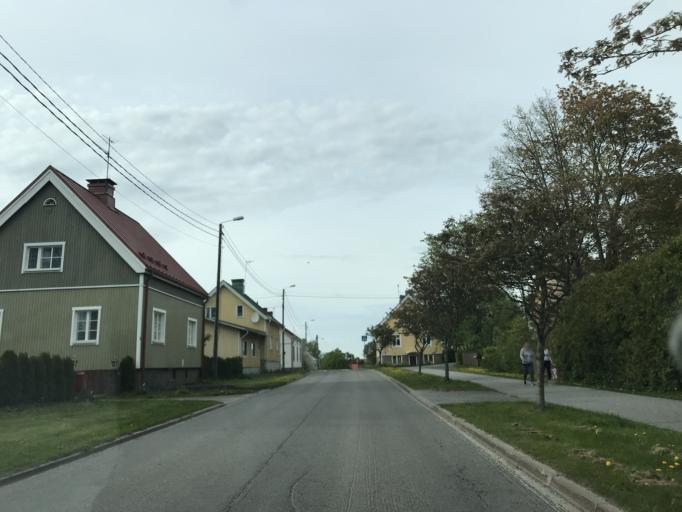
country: FI
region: Varsinais-Suomi
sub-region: Turku
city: Turku
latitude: 60.4528
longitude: 22.3082
